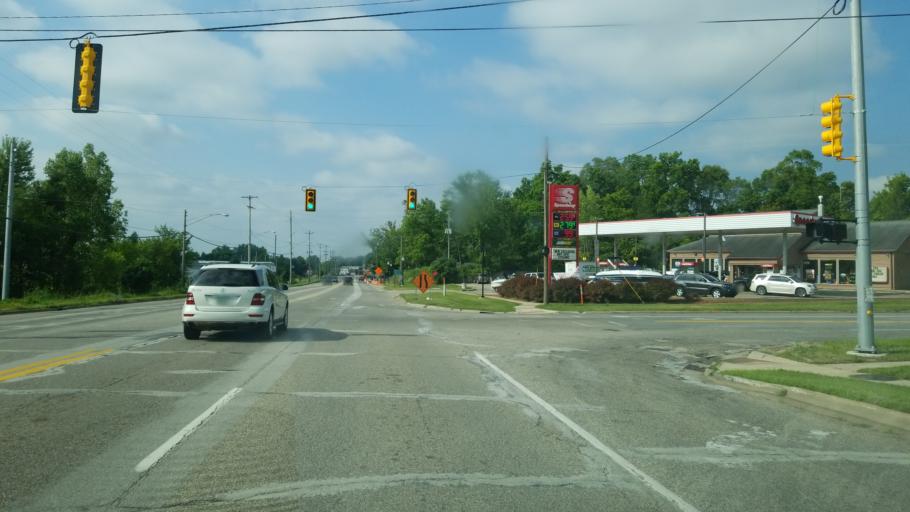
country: US
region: Michigan
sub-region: Kent County
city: Comstock Park
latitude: 43.0386
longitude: -85.6632
